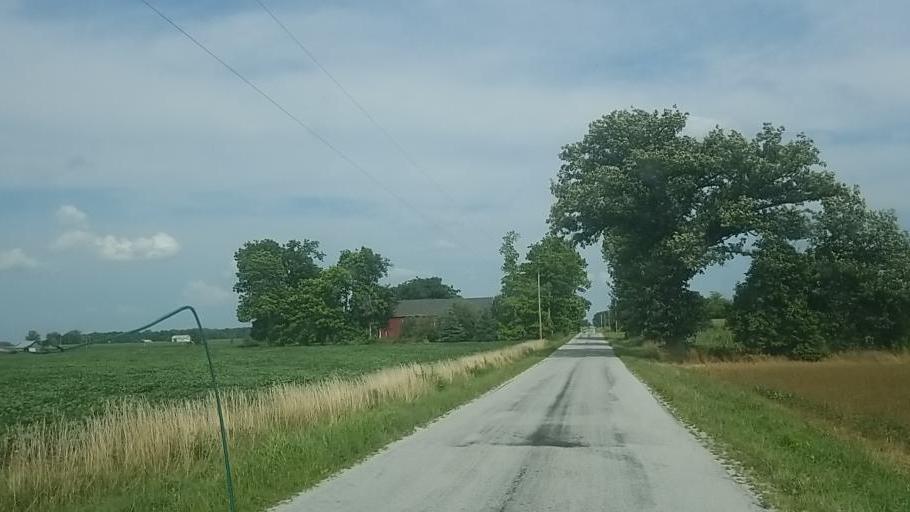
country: US
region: Ohio
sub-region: Hardin County
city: Forest
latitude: 40.8176
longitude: -83.4541
